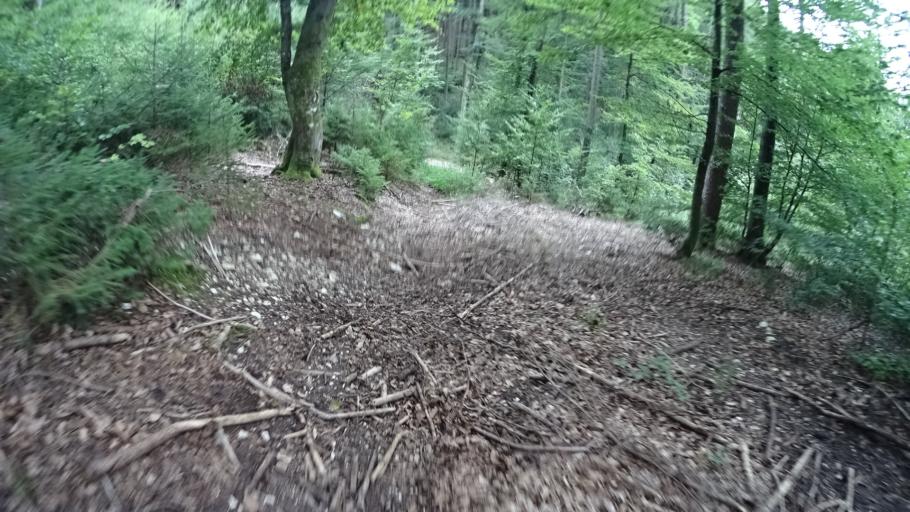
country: DE
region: Bavaria
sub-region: Upper Bavaria
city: Walting
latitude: 48.9125
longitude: 11.3101
